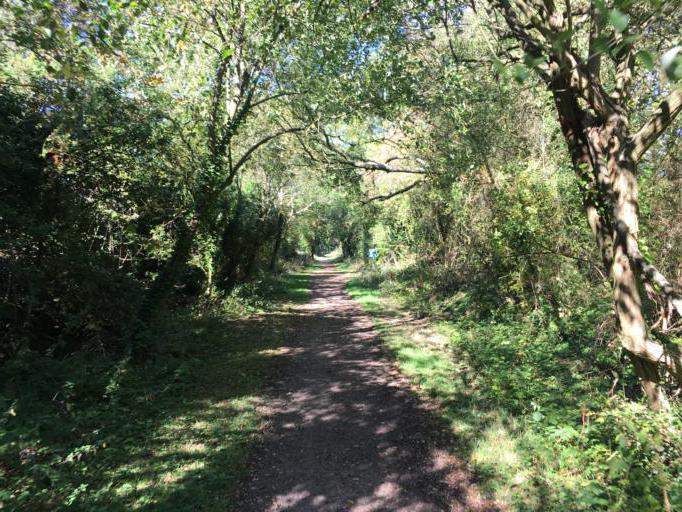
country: GB
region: England
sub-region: Solihull
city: Balsall Common
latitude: 52.3834
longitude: -1.6124
